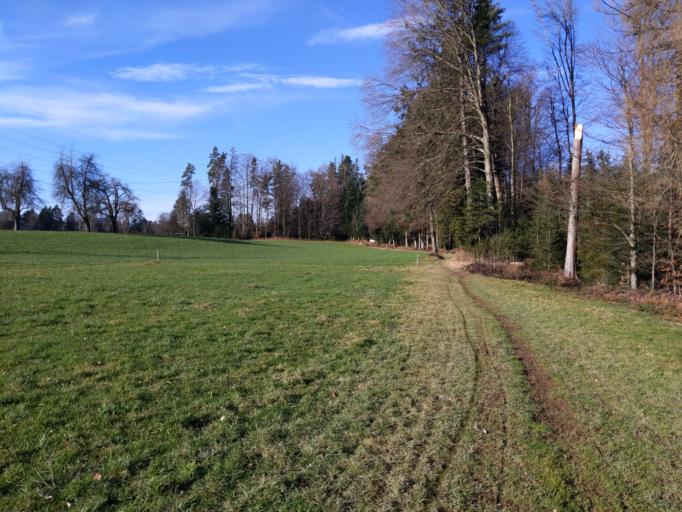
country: CH
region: Saint Gallen
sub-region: Wahlkreis See-Gaster
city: Schmerikon
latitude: 47.2327
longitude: 8.9365
